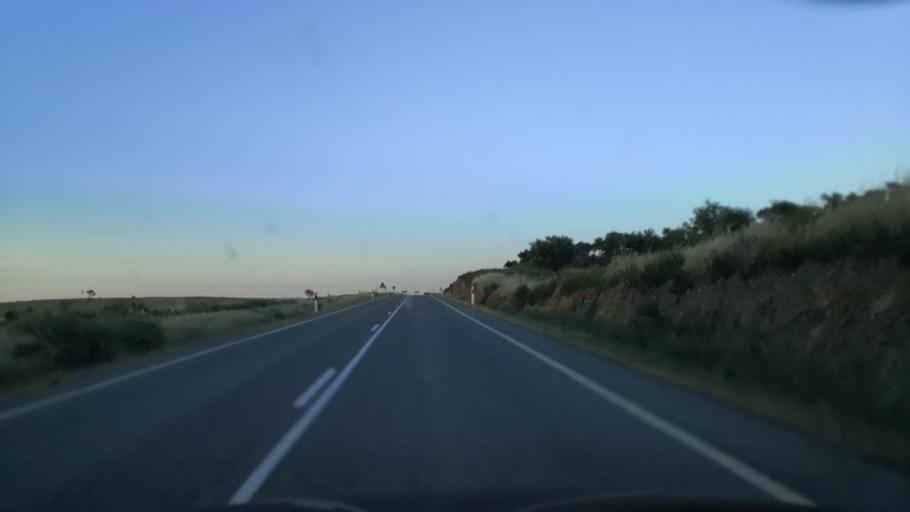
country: ES
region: Extremadura
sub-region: Provincia de Caceres
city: Salorino
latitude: 39.6054
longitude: -6.9731
